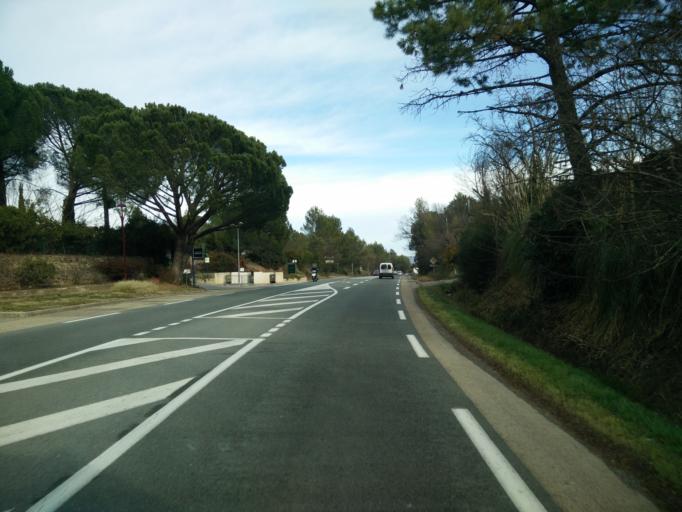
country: FR
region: Provence-Alpes-Cote d'Azur
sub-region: Departement du Var
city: Vidauban
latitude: 43.4338
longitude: 6.4393
